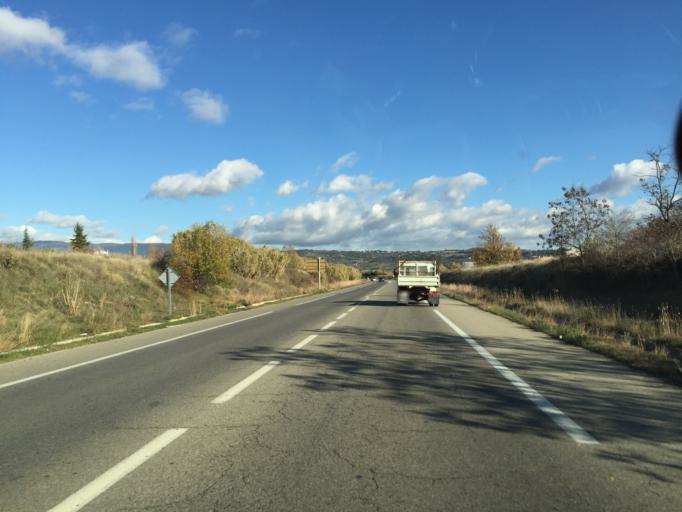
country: FR
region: Provence-Alpes-Cote d'Azur
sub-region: Departement du Vaucluse
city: Gargas
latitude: 43.8834
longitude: 5.3554
